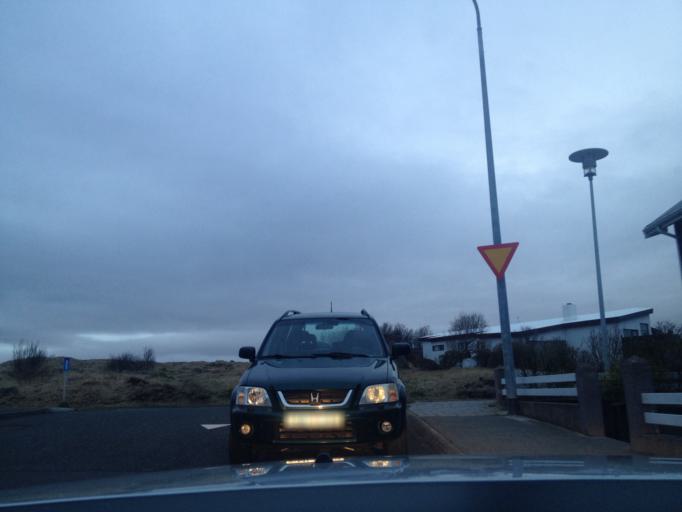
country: IS
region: Capital Region
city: Seltjarnarnes
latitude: 64.1541
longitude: -21.9987
